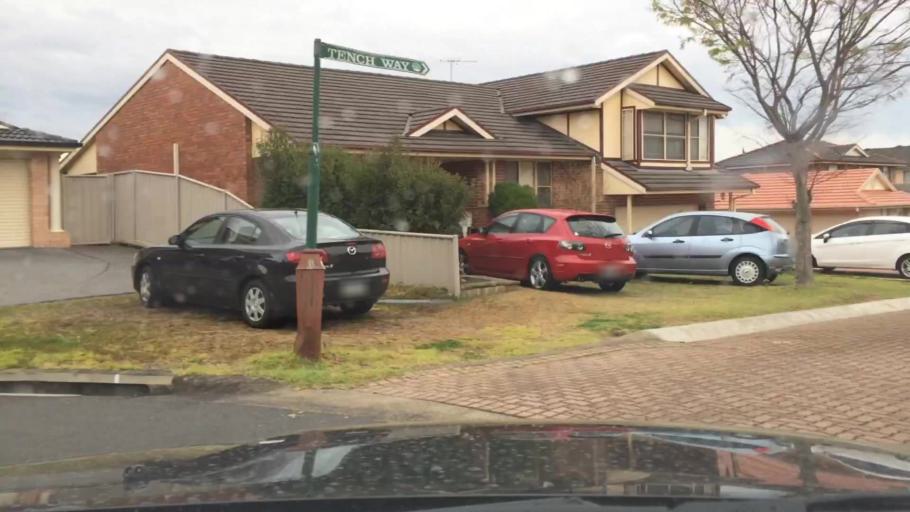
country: AU
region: New South Wales
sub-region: Campbelltown Municipality
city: Denham Court
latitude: -33.9390
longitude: 150.8334
